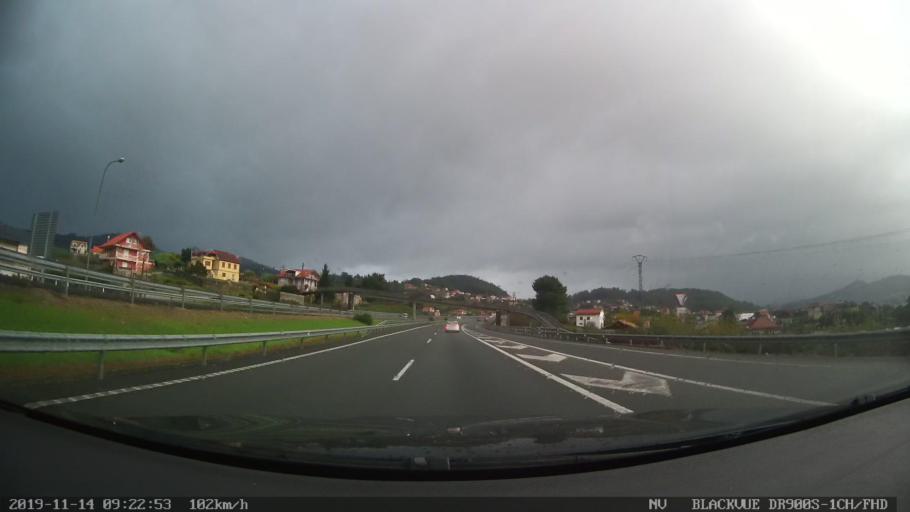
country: ES
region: Galicia
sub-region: Provincia de Pontevedra
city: Redondela
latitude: 42.3207
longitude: -8.6596
